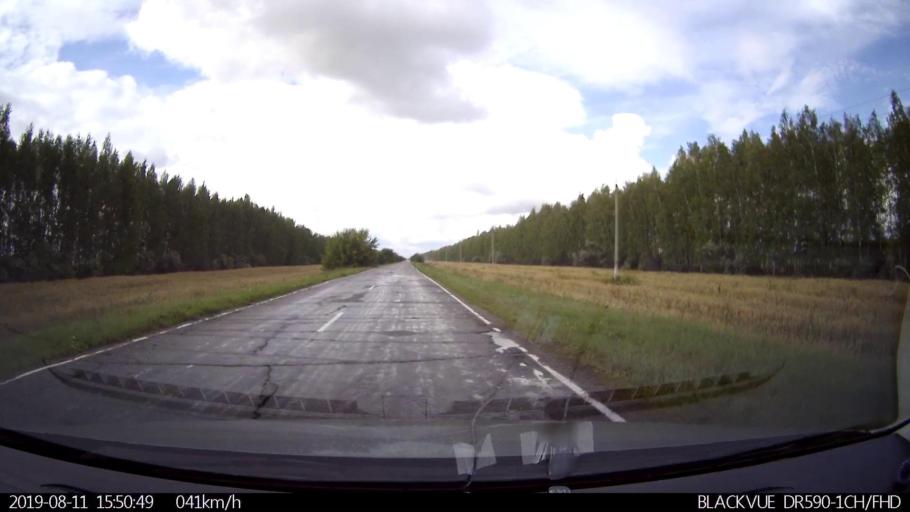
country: RU
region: Ulyanovsk
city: Ignatovka
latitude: 53.9142
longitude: 47.6559
